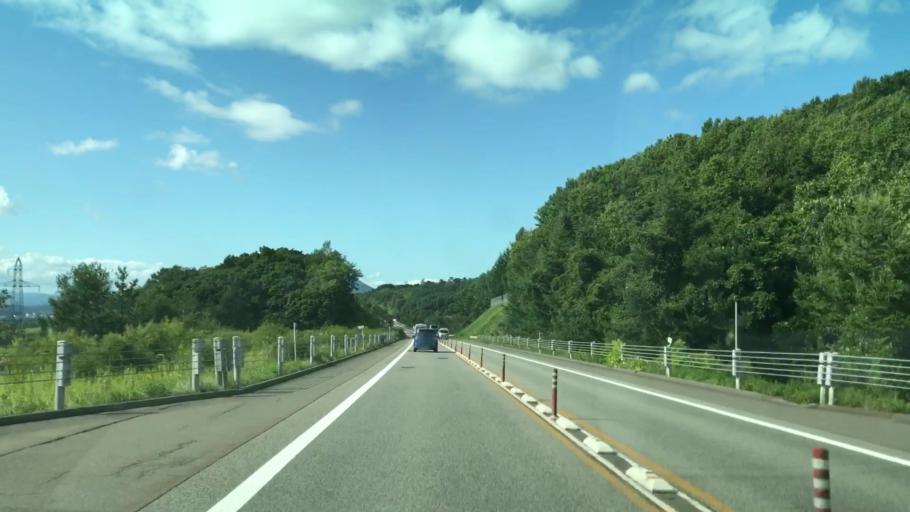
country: JP
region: Hokkaido
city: Date
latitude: 42.4295
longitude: 140.9257
